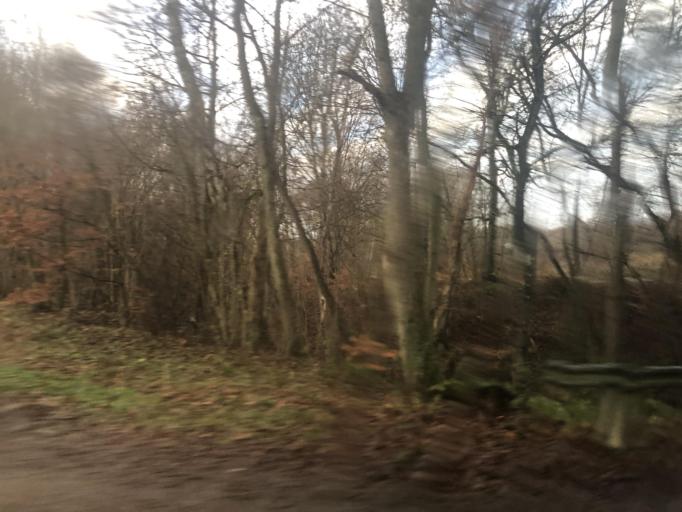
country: SE
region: Skane
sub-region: Lunds Kommun
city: Veberod
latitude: 55.6042
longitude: 13.5387
